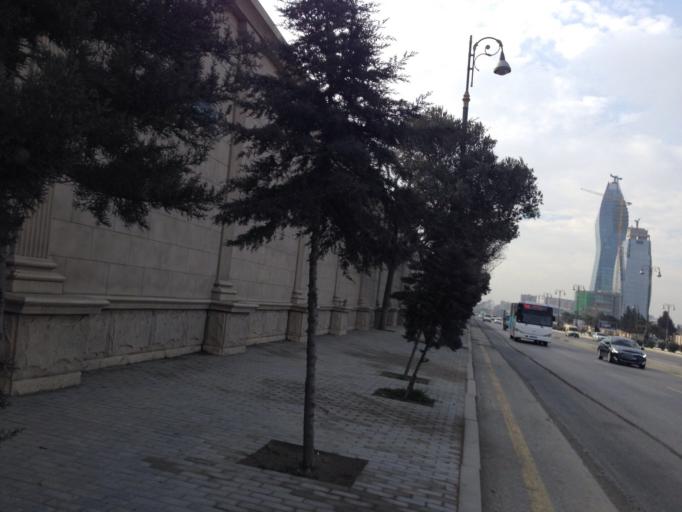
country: AZ
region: Baki
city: Baku
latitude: 40.4093
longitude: 49.8932
